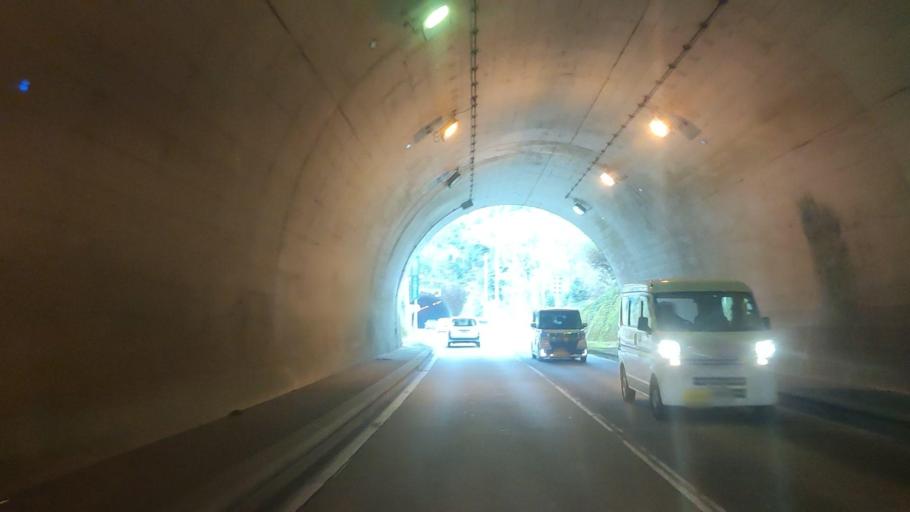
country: JP
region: Nagasaki
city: Shimabara
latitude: 32.8329
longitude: 130.2113
